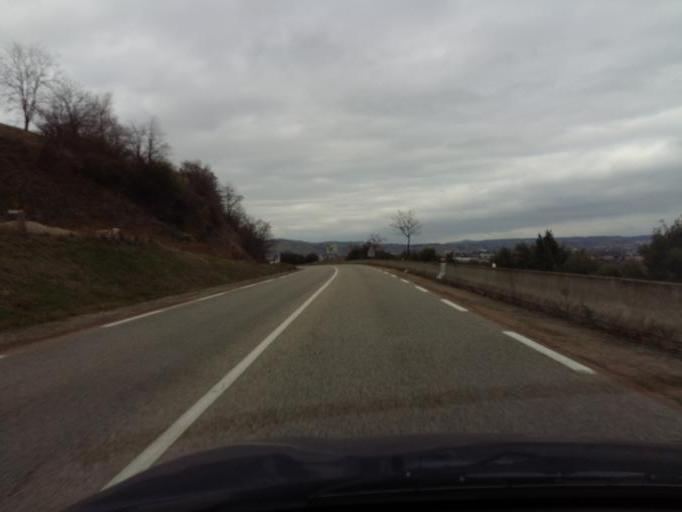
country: FR
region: Rhone-Alpes
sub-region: Departement de l'Ardeche
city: Mauves
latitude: 45.0402
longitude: 4.8263
